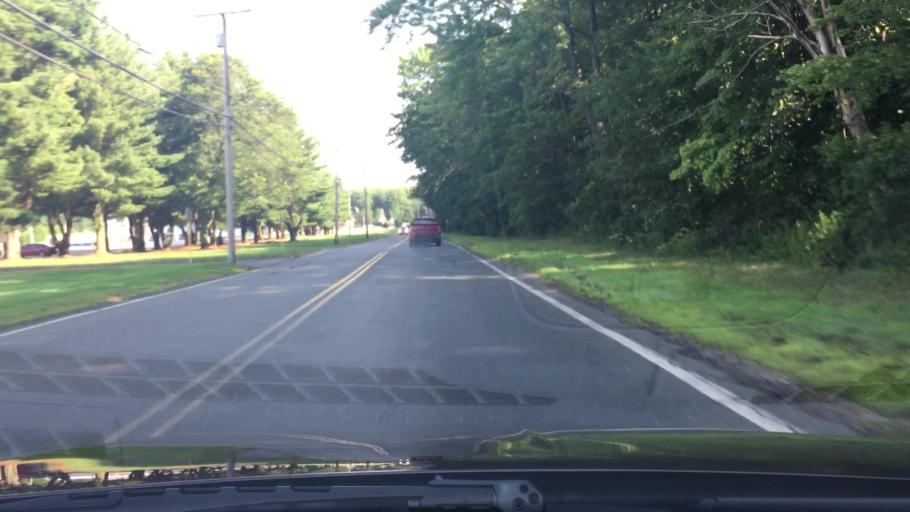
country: US
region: Massachusetts
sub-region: Hampden County
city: East Longmeadow
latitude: 42.0441
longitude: -72.5183
